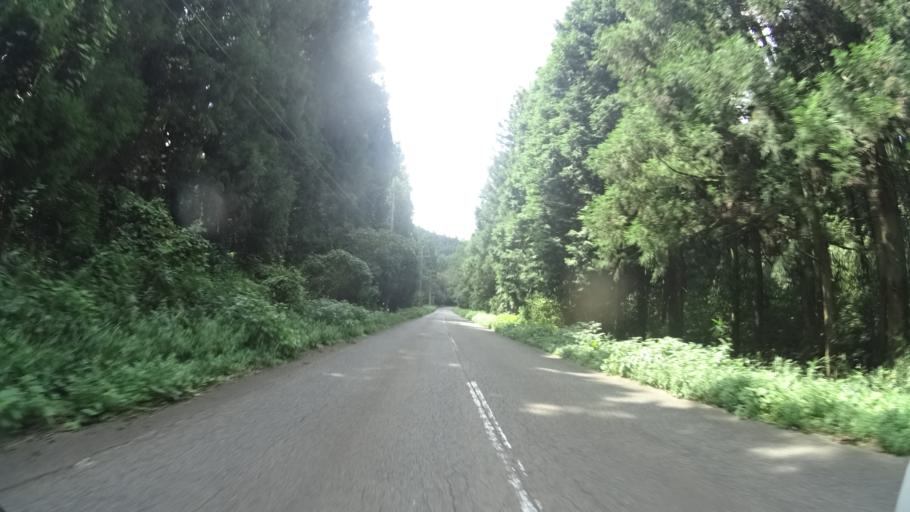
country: JP
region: Yamaguchi
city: Hagi
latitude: 34.5101
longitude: 131.5918
